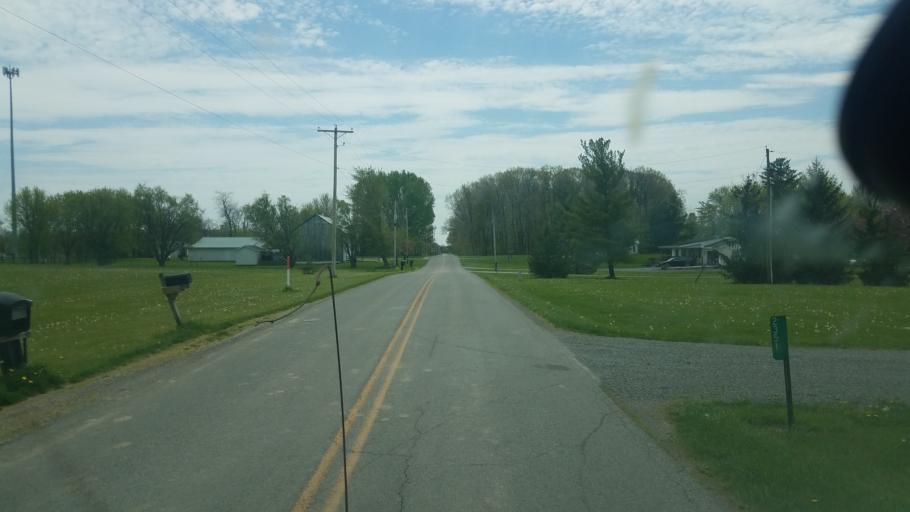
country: US
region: Ohio
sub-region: Allen County
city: Lima
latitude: 40.7756
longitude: -83.9665
